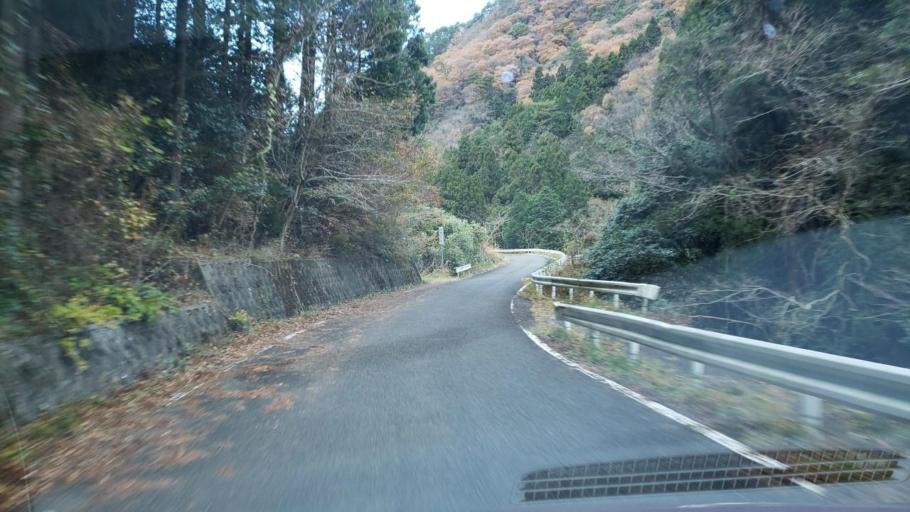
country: JP
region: Tokushima
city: Wakimachi
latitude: 34.1437
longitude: 134.2287
